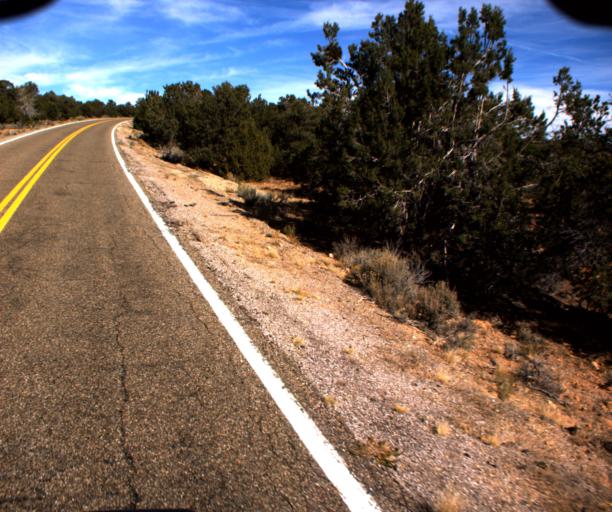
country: US
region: Arizona
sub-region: Navajo County
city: Kayenta
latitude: 36.6245
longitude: -110.5092
